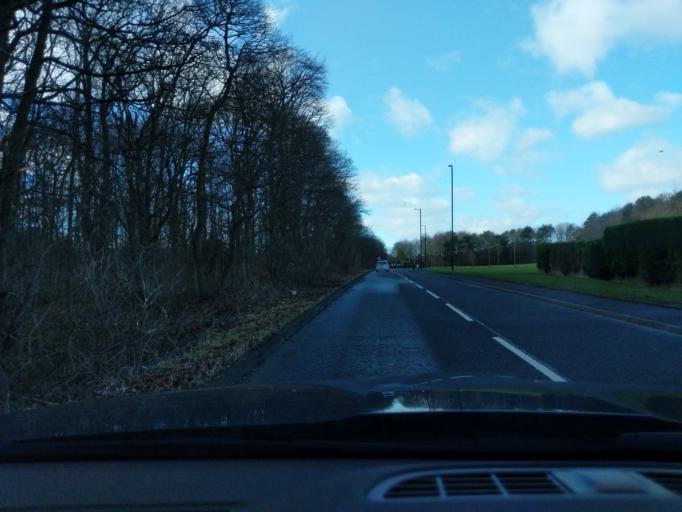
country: GB
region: England
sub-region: Sunderland
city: Washington
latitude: 54.8781
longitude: -1.5417
